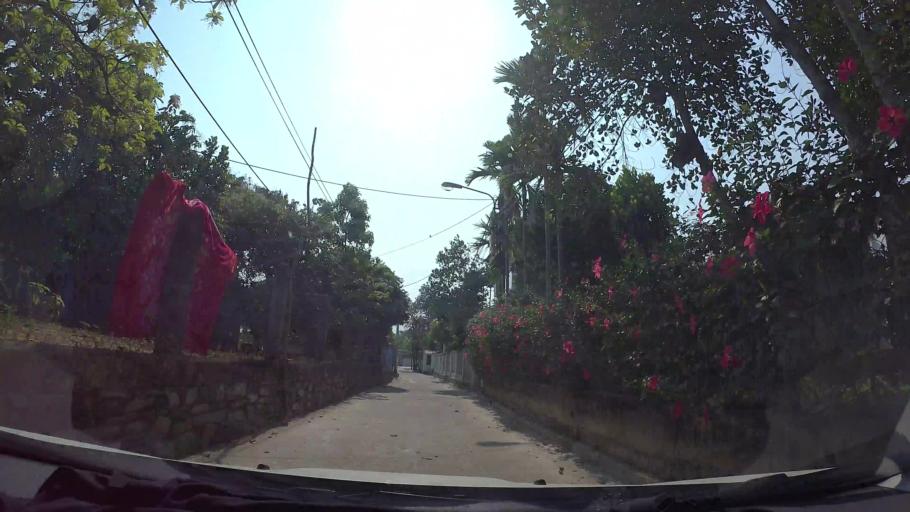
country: VN
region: Da Nang
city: Cam Le
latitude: 16.0048
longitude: 108.1937
